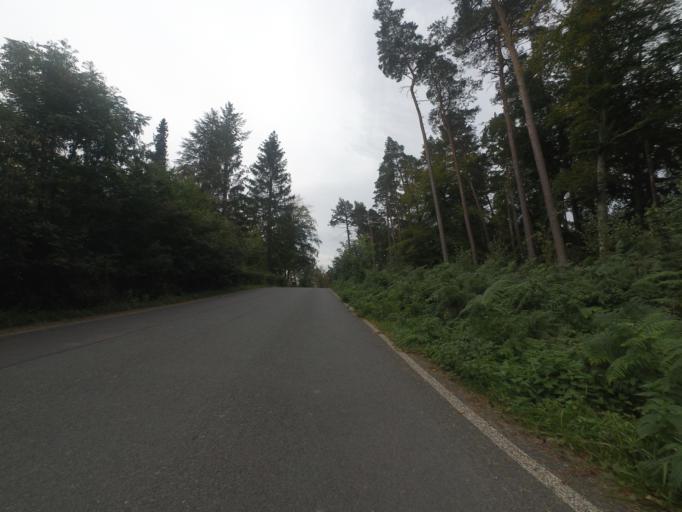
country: DE
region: North Rhine-Westphalia
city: Iserlohn
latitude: 51.4047
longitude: 7.6778
